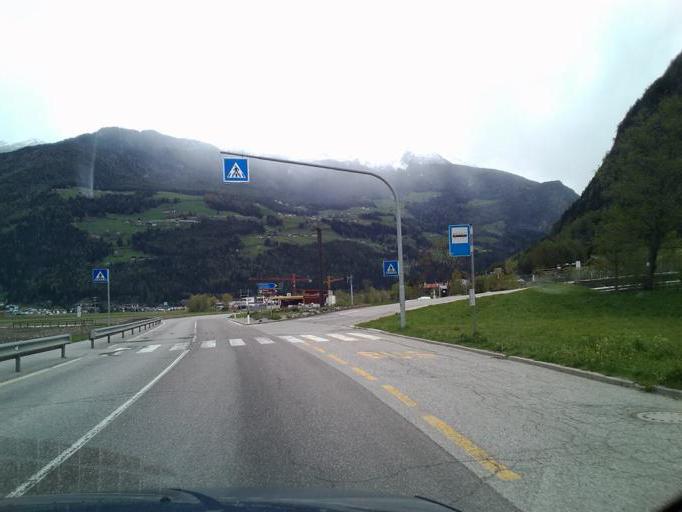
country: IT
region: Trentino-Alto Adige
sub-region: Bolzano
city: Campo Tures
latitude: 46.9029
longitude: 11.9553
